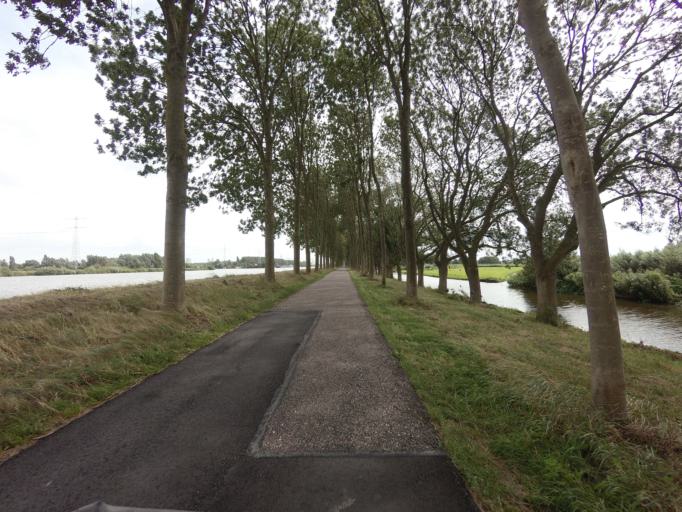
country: NL
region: North Holland
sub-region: Gemeente Diemen
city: Diemen
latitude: 52.3438
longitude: 4.9941
